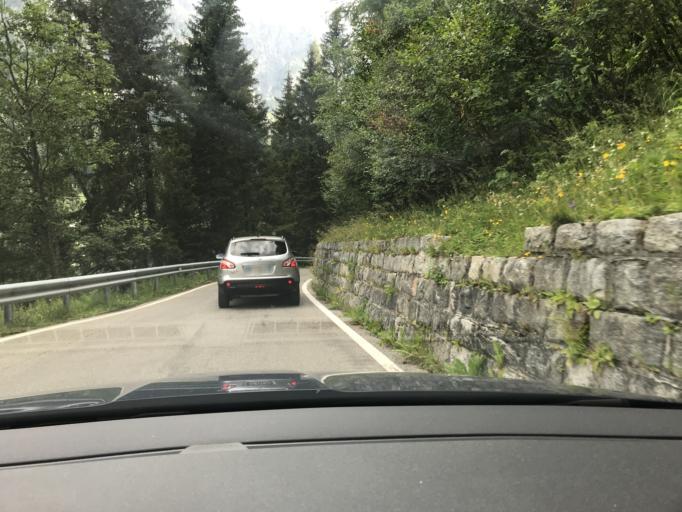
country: IT
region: Trentino-Alto Adige
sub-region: Bolzano
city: San Martino
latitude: 46.8839
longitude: 12.1691
